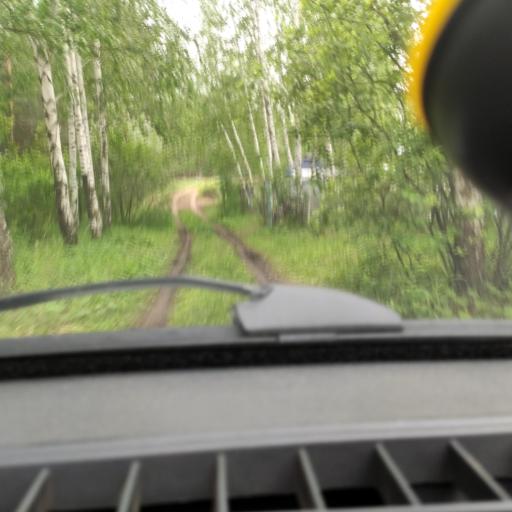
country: RU
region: Samara
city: Zhigulevsk
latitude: 53.5040
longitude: 49.5015
